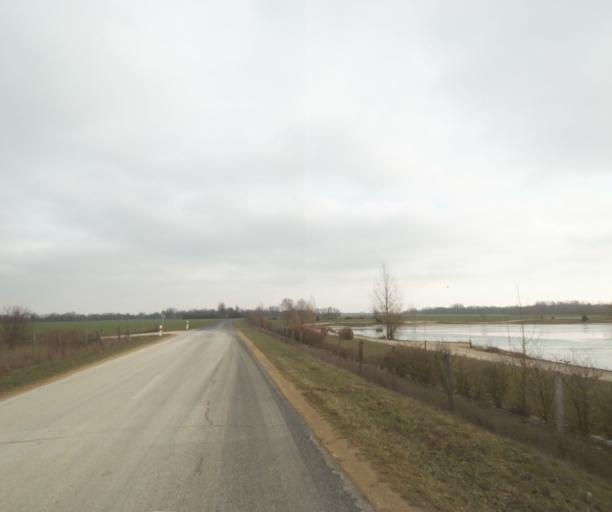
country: FR
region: Champagne-Ardenne
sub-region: Departement de la Haute-Marne
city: Villiers-en-Lieu
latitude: 48.6533
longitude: 4.7766
